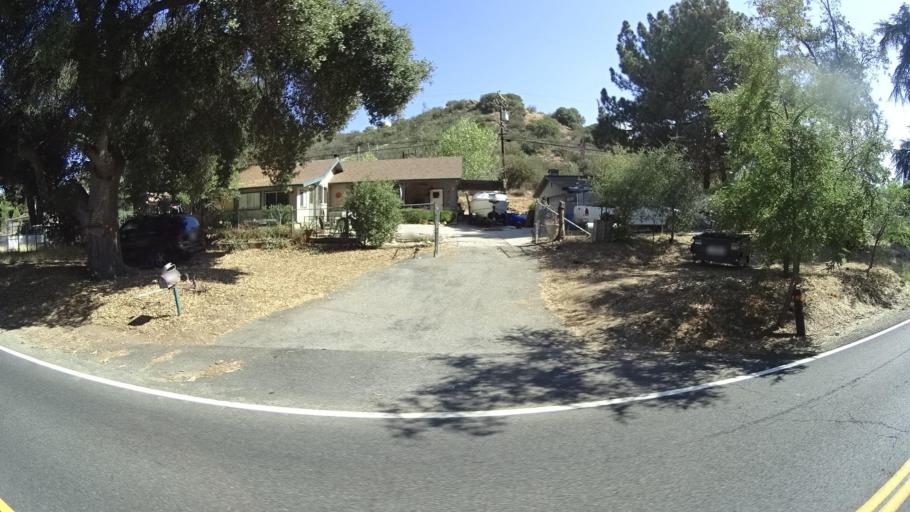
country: US
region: California
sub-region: Riverside County
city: Aguanga
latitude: 33.3494
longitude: -116.7354
